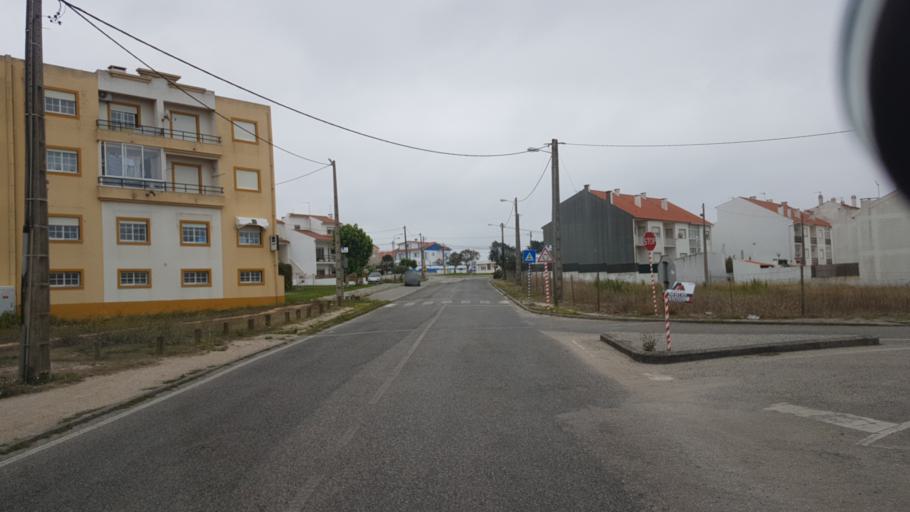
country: PT
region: Lisbon
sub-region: Torres Vedras
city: Silveira
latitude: 39.1457
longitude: -9.3640
